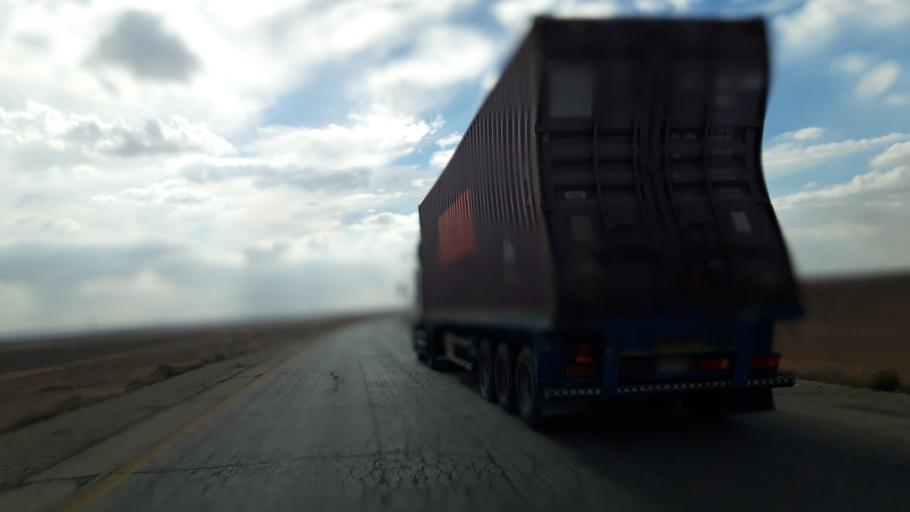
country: JO
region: Amman
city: Al Azraq ash Shamali
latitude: 31.7324
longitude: 36.5096
